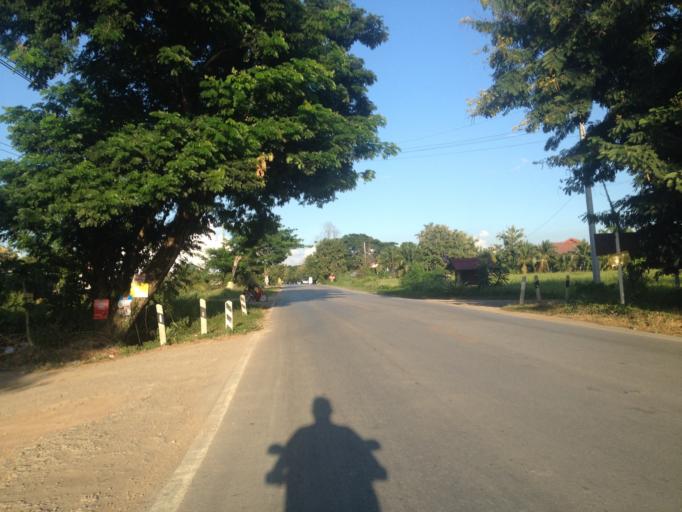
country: TH
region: Chiang Mai
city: San Pa Tong
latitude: 18.6144
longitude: 98.8582
